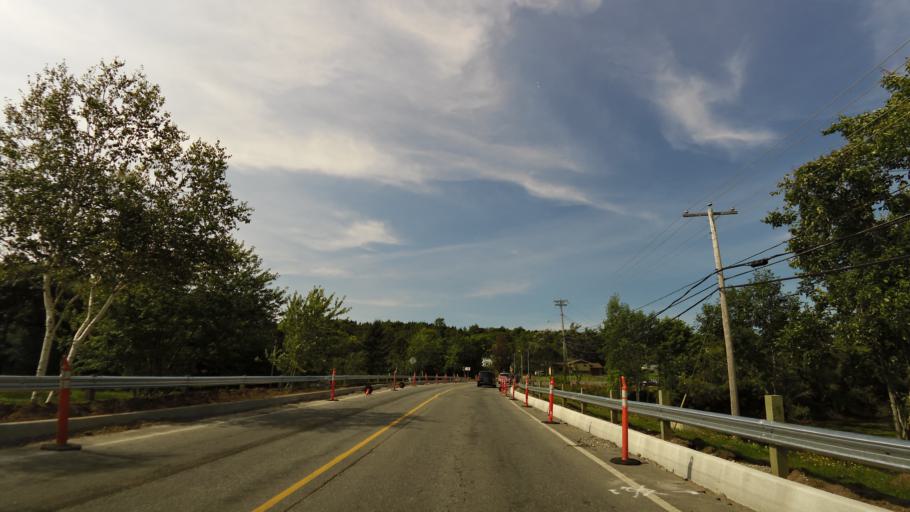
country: CA
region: New Brunswick
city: Hampton
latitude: 45.5270
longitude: -65.8299
